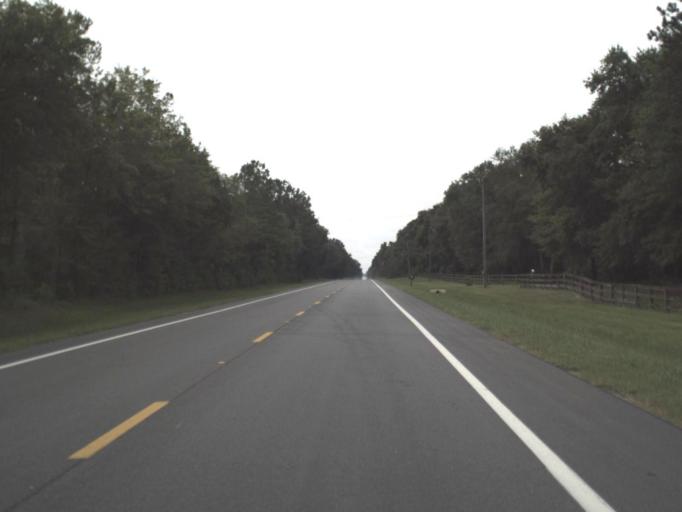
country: US
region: Florida
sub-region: Columbia County
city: Five Points
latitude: 30.4384
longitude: -82.6447
